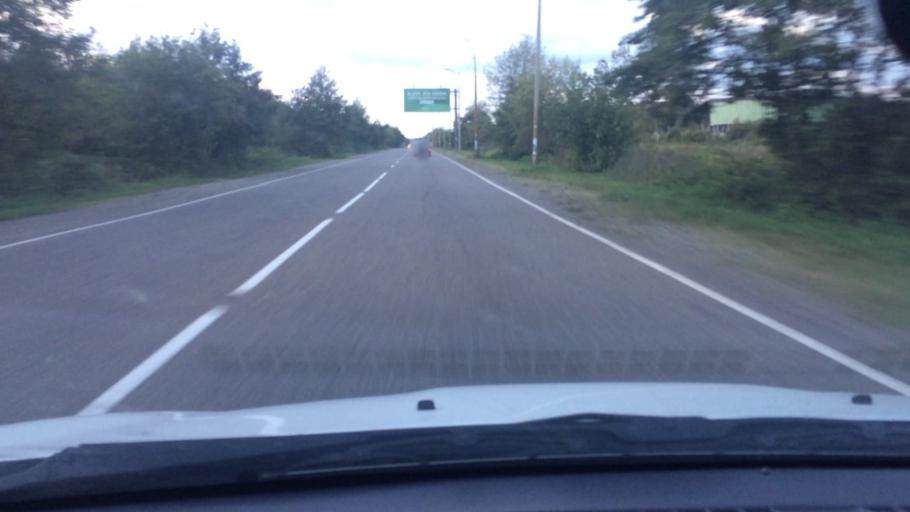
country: GE
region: Guria
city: Urek'i
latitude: 41.9329
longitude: 41.7723
